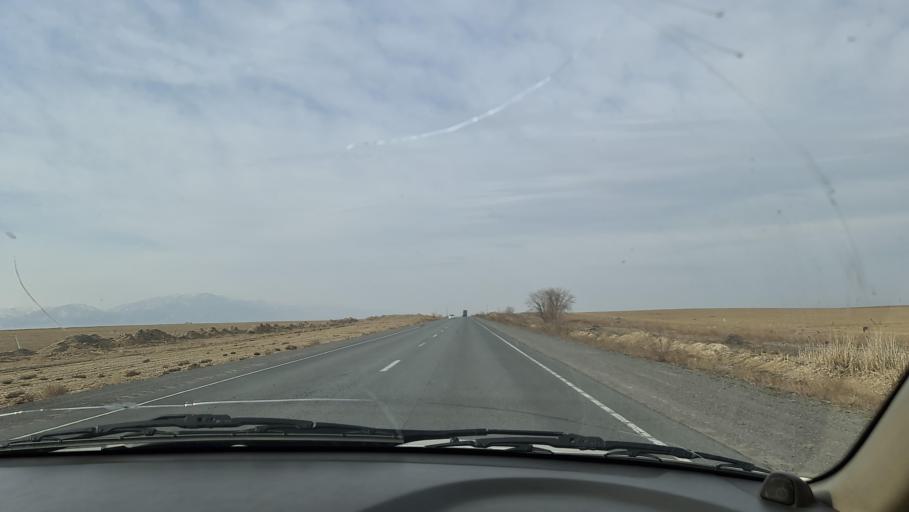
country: KG
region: Chuy
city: Bystrovka
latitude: 43.3244
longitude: 75.7001
